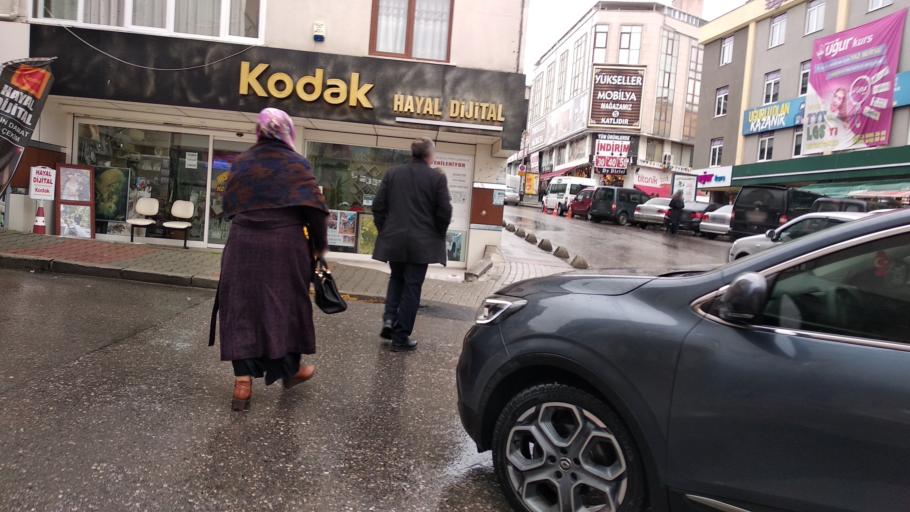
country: TR
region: Istanbul
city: Samandira
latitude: 41.0158
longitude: 29.1905
